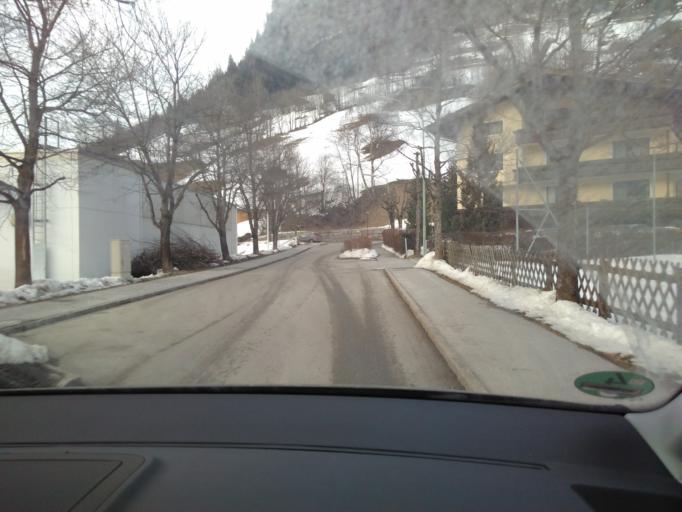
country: AT
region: Salzburg
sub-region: Politischer Bezirk Sankt Johann im Pongau
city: Bad Hofgastein
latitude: 47.1786
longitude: 13.1030
